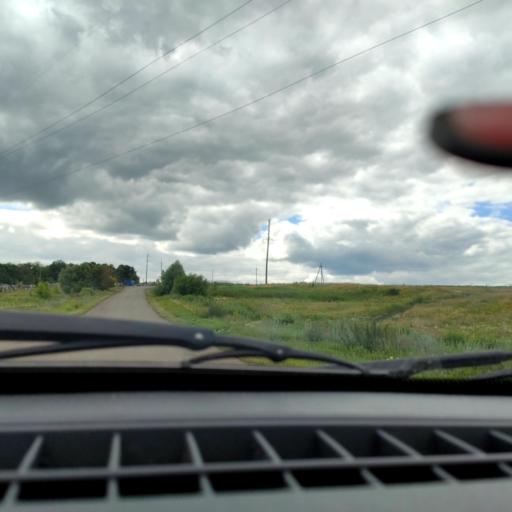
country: RU
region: Bashkortostan
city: Avdon
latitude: 54.7084
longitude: 55.8008
